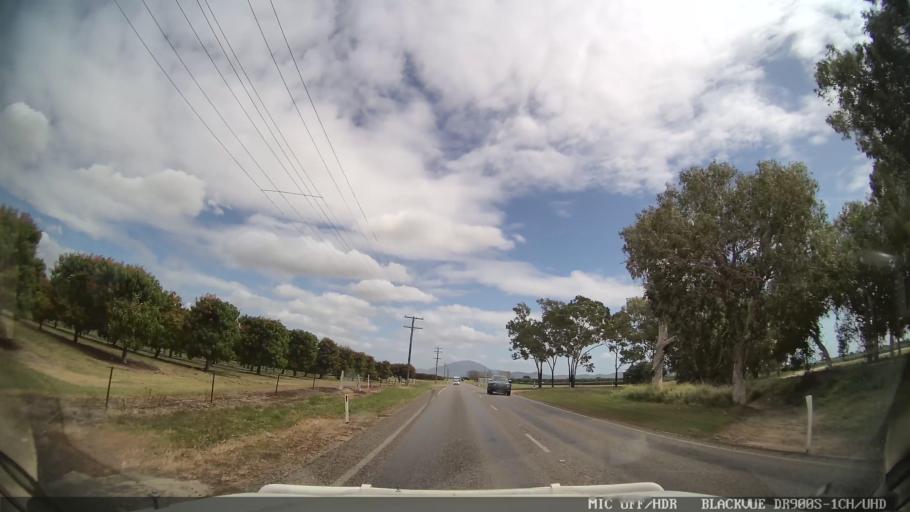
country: AU
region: Queensland
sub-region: Whitsunday
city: Bowen
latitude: -20.0159
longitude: 148.1867
